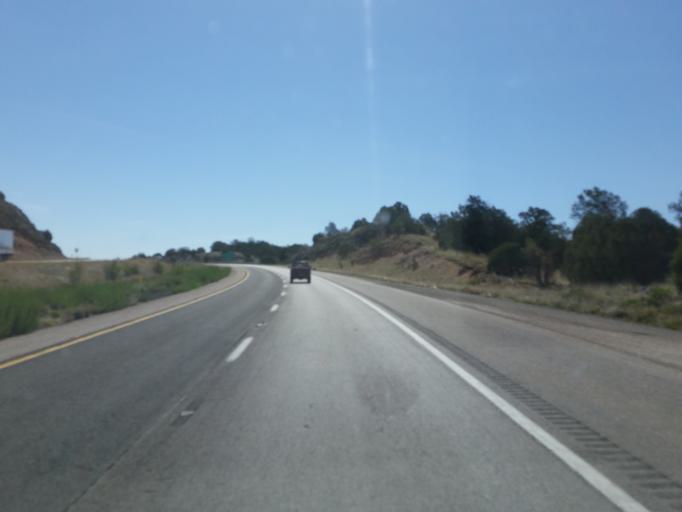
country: US
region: Arizona
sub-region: Mohave County
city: Peach Springs
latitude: 35.2855
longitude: -113.0989
